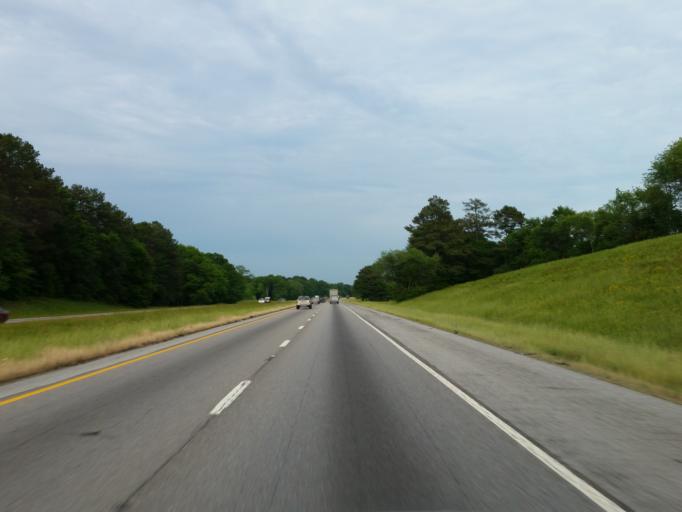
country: US
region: Alabama
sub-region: Talladega County
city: Lincoln
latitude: 33.5852
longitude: -86.0550
